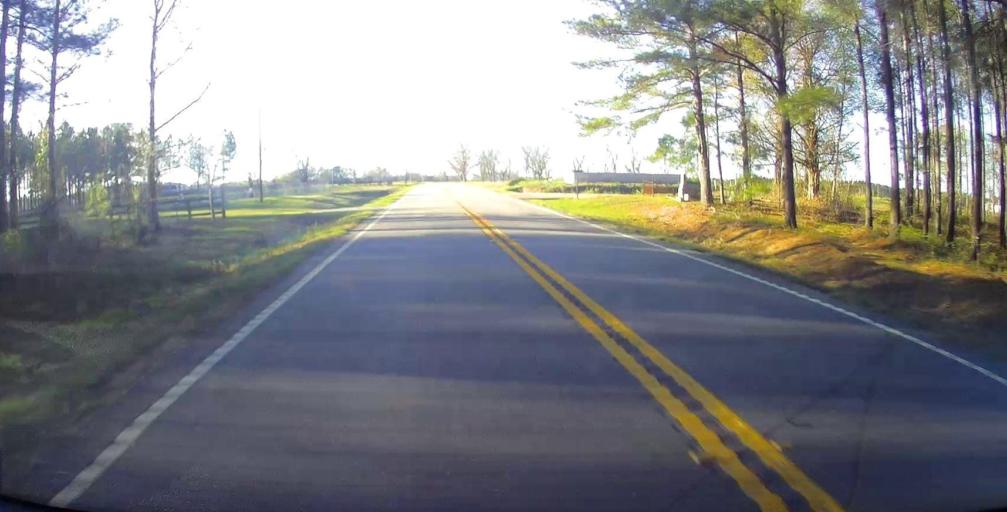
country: US
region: Georgia
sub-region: Wilcox County
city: Abbeville
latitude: 32.1443
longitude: -83.3453
